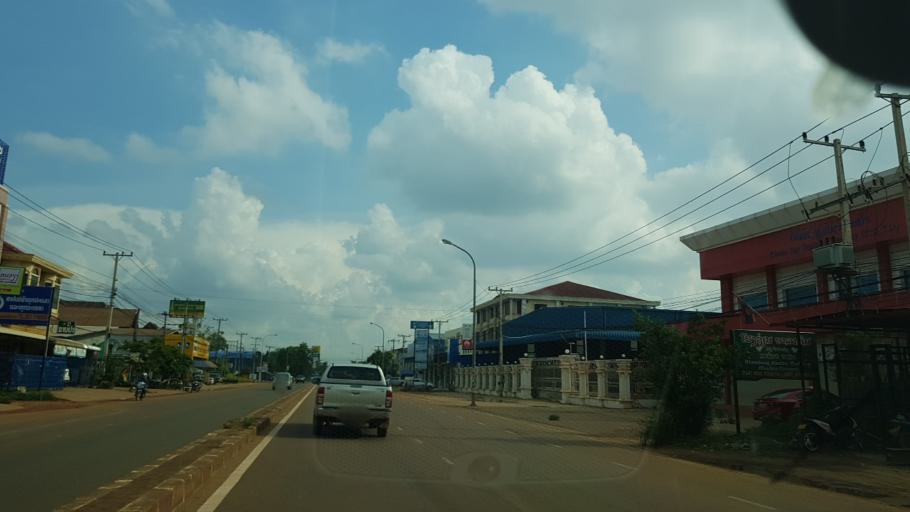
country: LA
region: Vientiane
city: Vientiane
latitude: 18.0217
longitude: 102.6514
